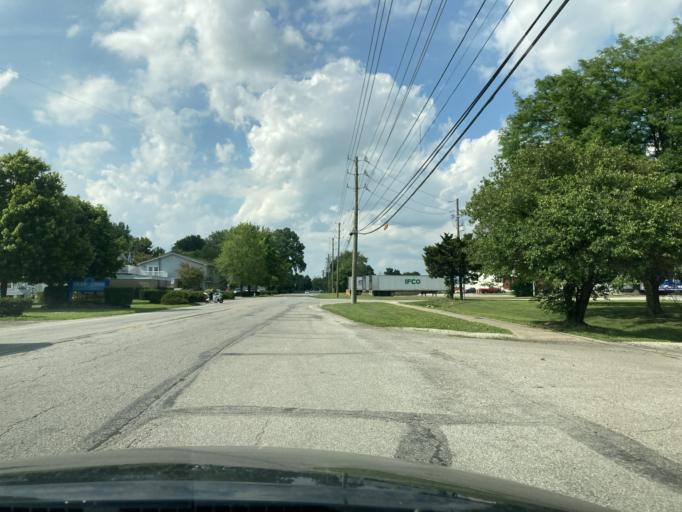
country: US
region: Indiana
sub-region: Marion County
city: Speedway
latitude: 39.8606
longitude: -86.2317
